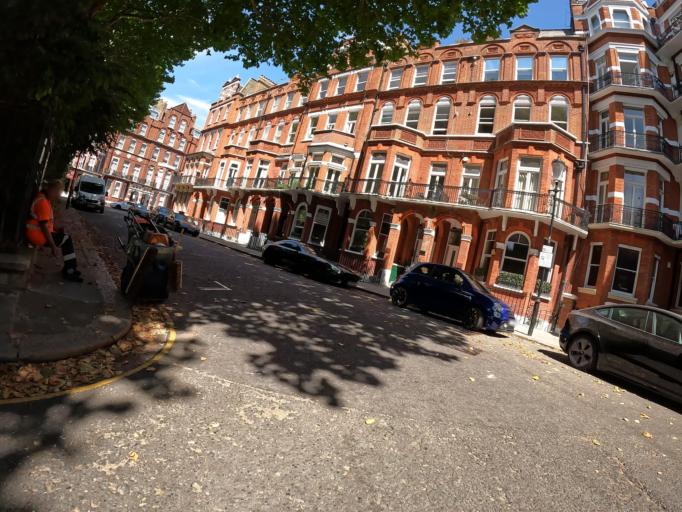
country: GB
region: England
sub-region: Greater London
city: Kensington
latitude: 51.4918
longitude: -0.1905
